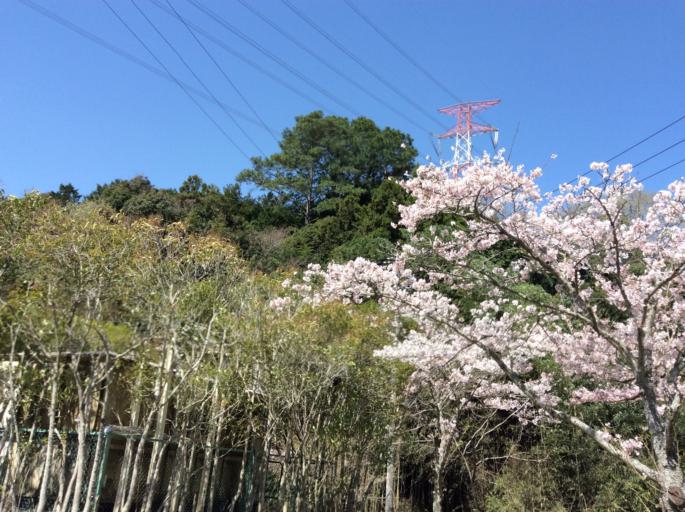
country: JP
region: Shizuoka
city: Kanaya
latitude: 34.7852
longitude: 138.1175
